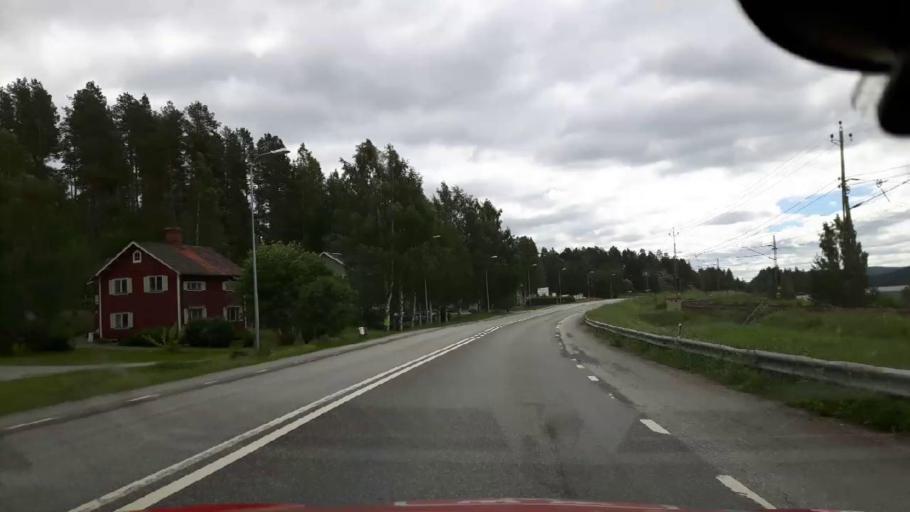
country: SE
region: Jaemtland
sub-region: Braecke Kommun
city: Braecke
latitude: 62.7444
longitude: 15.4252
